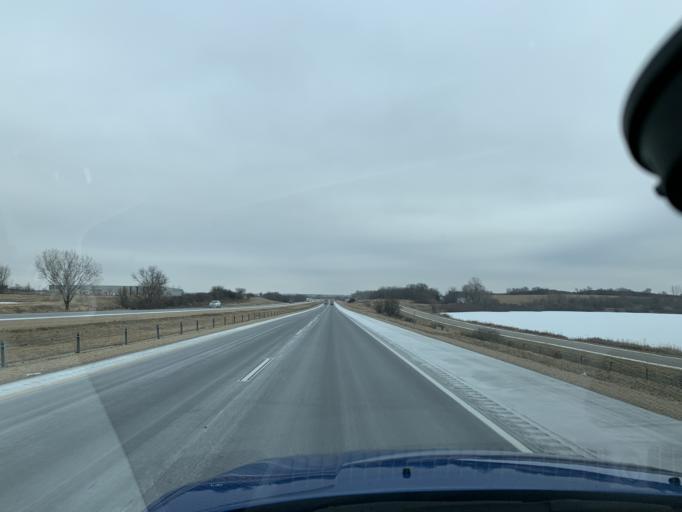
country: US
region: Wisconsin
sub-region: Dane County
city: Sun Prairie
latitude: 43.2045
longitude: -89.1865
